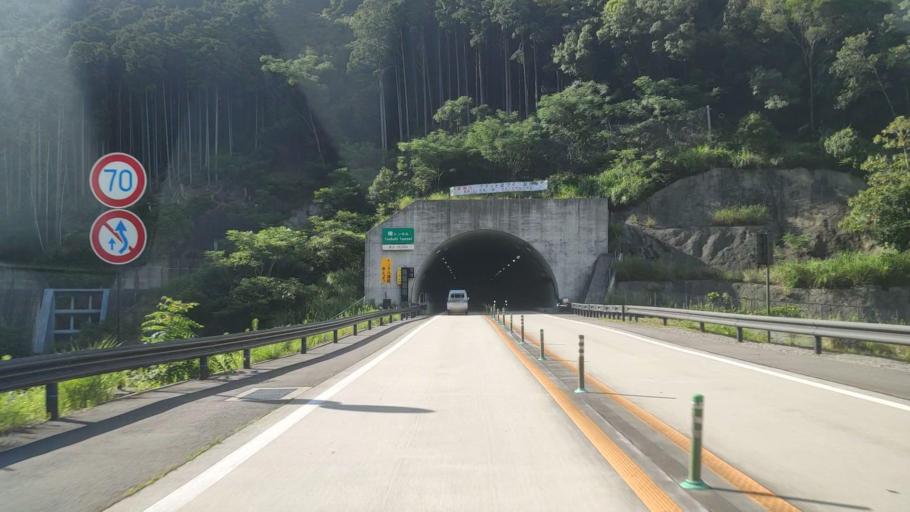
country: JP
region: Wakayama
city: Tanabe
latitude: 33.5992
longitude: 135.4328
